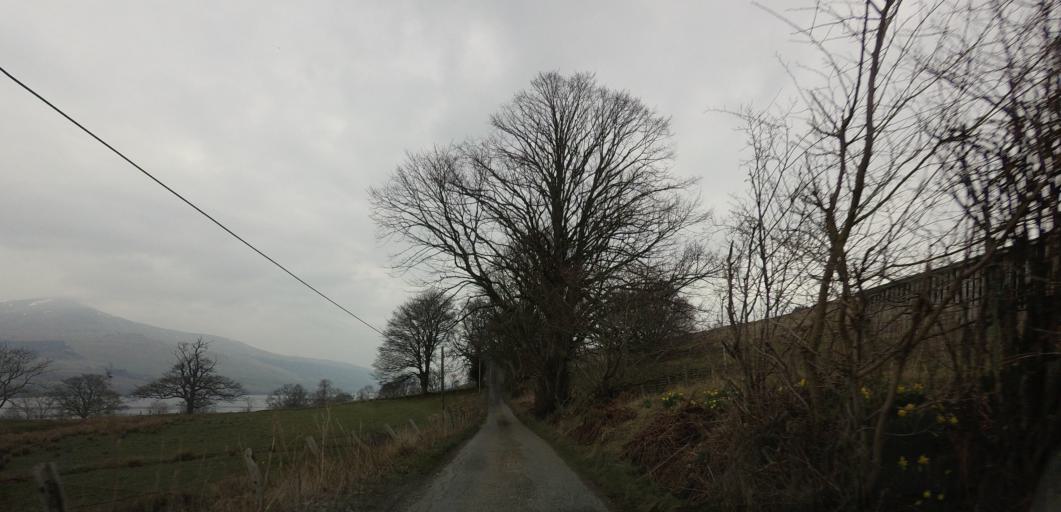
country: GB
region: Scotland
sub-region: Perth and Kinross
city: Comrie
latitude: 56.5091
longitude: -4.1371
